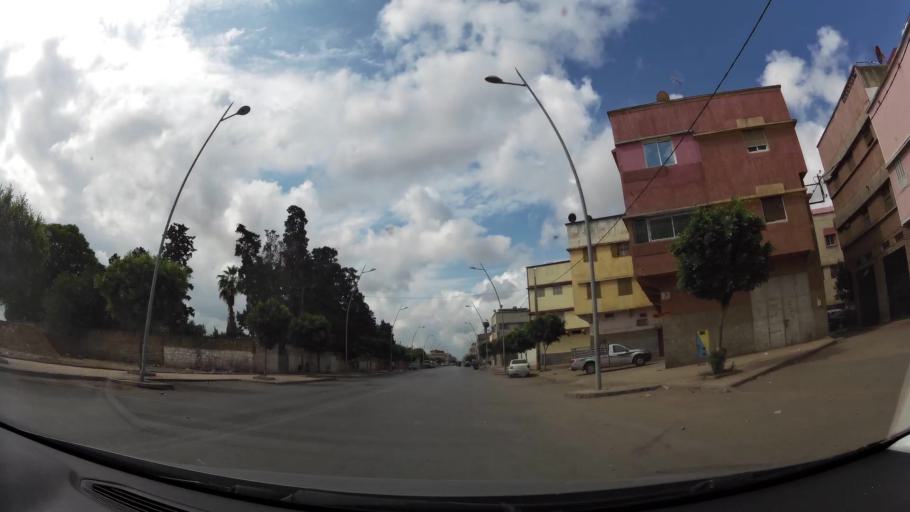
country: MA
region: Gharb-Chrarda-Beni Hssen
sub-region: Kenitra Province
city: Kenitra
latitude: 34.2697
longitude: -6.5586
